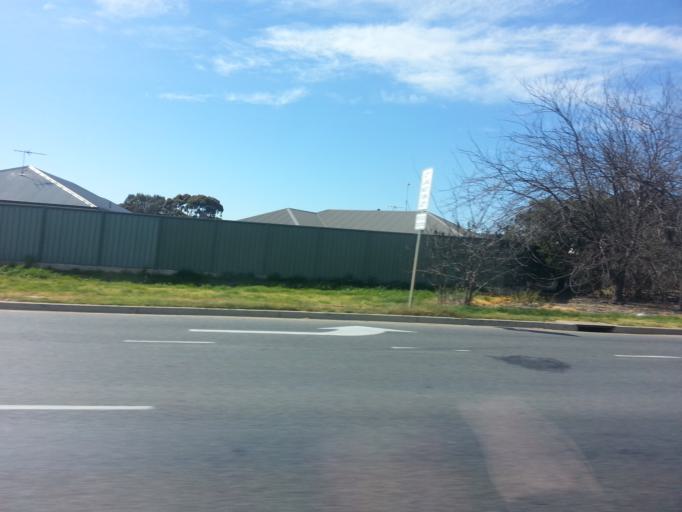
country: AU
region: South Australia
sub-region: Salisbury
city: Salisbury
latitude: -34.7617
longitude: 138.5925
